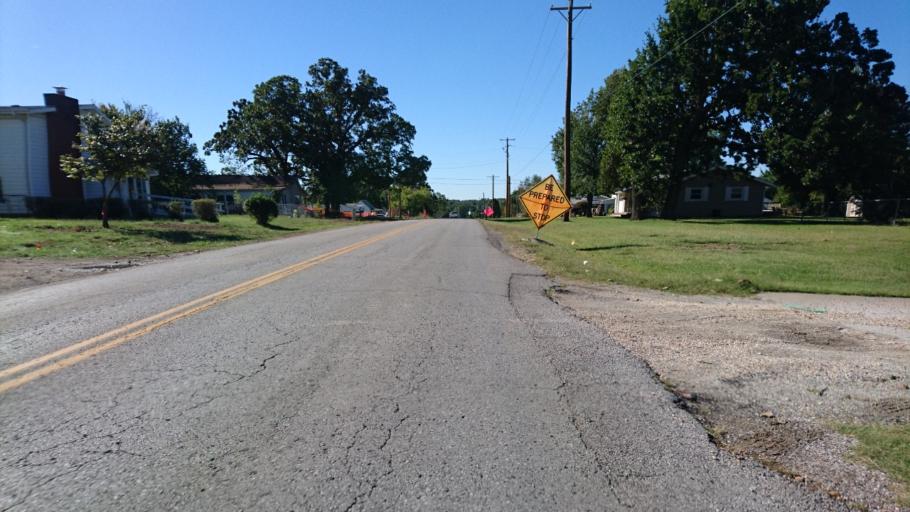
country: US
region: Missouri
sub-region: Jasper County
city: Joplin
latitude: 37.1091
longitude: -94.4943
